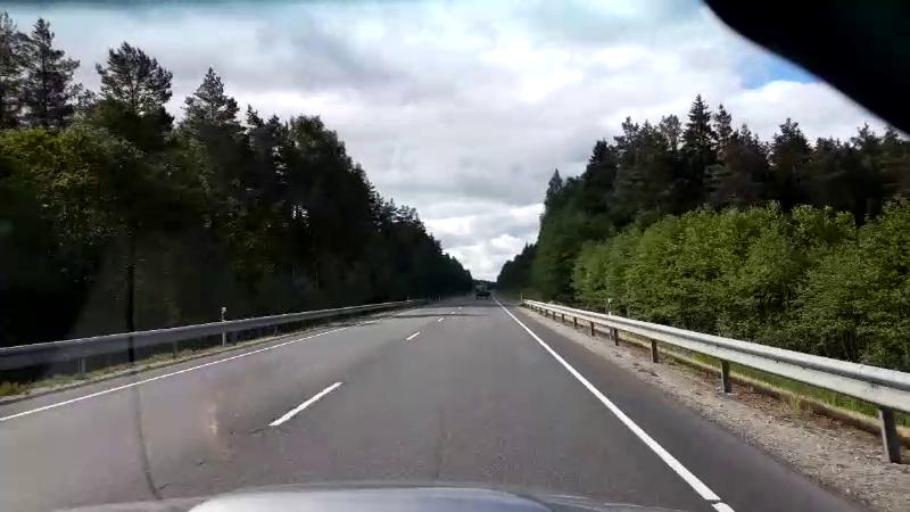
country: EE
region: Raplamaa
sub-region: Maerjamaa vald
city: Marjamaa
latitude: 58.9031
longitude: 24.4558
